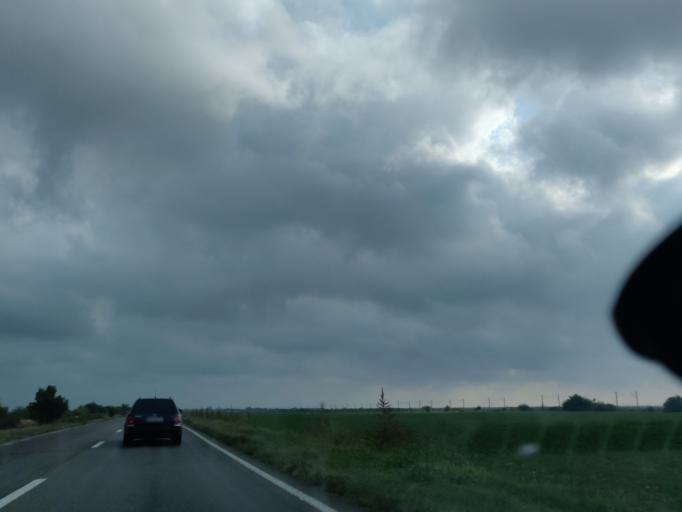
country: RO
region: Prahova
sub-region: Oras Mizil
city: Mizil
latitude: 45.0132
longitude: 26.4707
